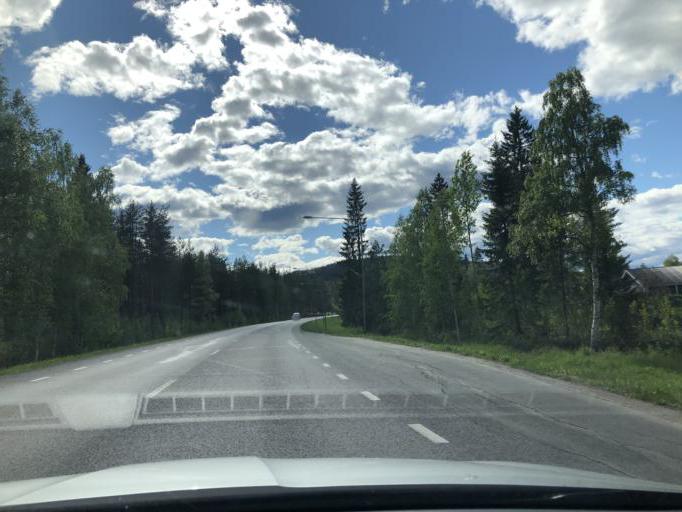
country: SE
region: Norrbotten
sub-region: Alvsbyns Kommun
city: AElvsbyn
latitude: 65.6672
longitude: 20.9901
